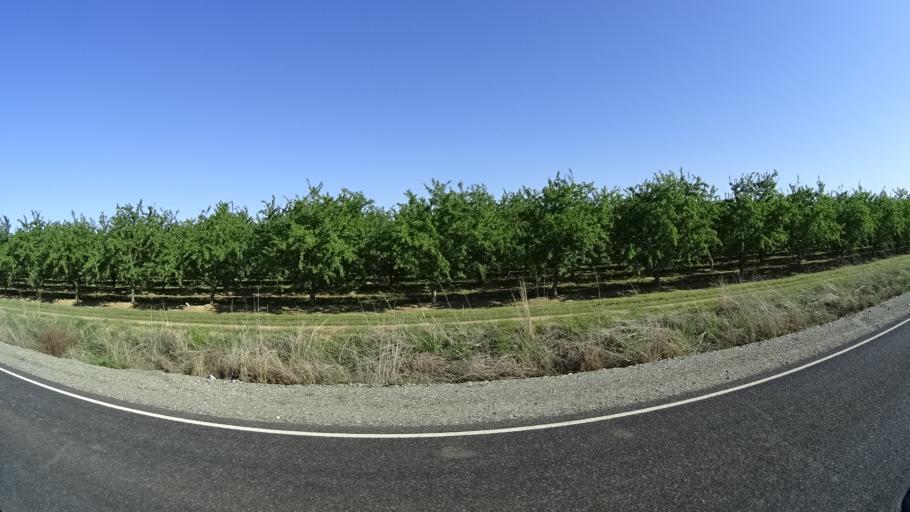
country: US
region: California
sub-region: Glenn County
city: Hamilton City
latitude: 39.7665
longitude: -122.0743
